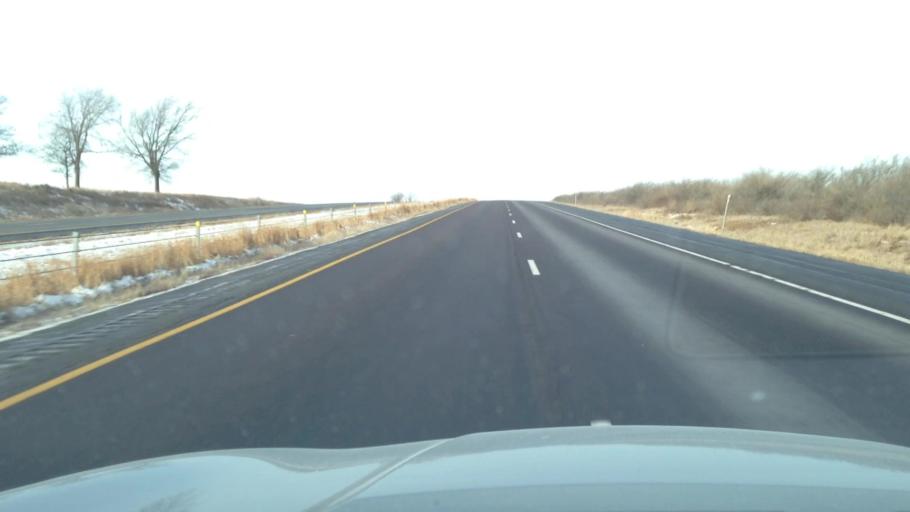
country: US
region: Iowa
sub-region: Poweshiek County
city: Grinnell
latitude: 41.6959
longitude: -92.6542
